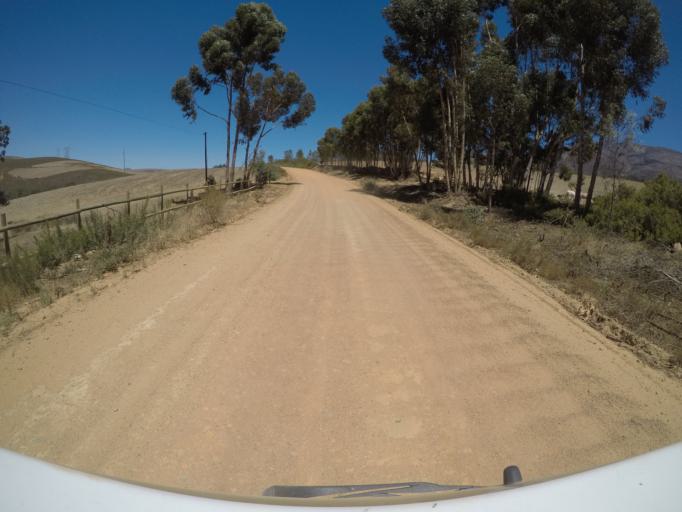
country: ZA
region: Western Cape
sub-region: Overberg District Municipality
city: Caledon
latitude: -34.1950
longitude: 19.2232
